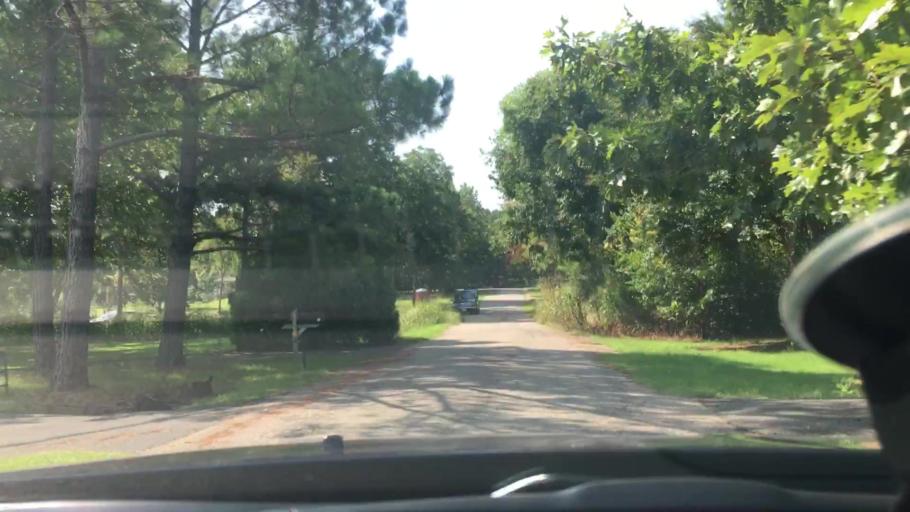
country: US
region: Oklahoma
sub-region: Bryan County
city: Durant
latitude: 34.0482
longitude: -96.3794
